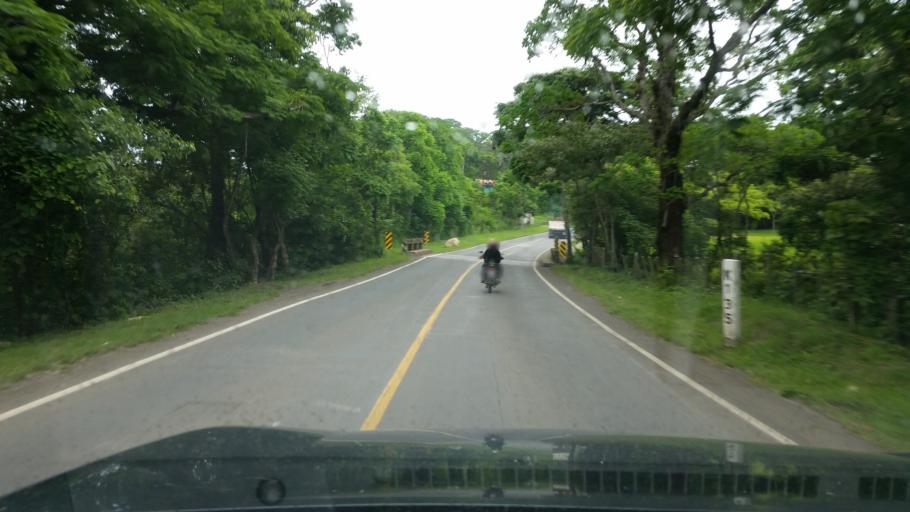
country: NI
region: Matagalpa
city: Matagalpa
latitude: 12.9409
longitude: -85.8849
